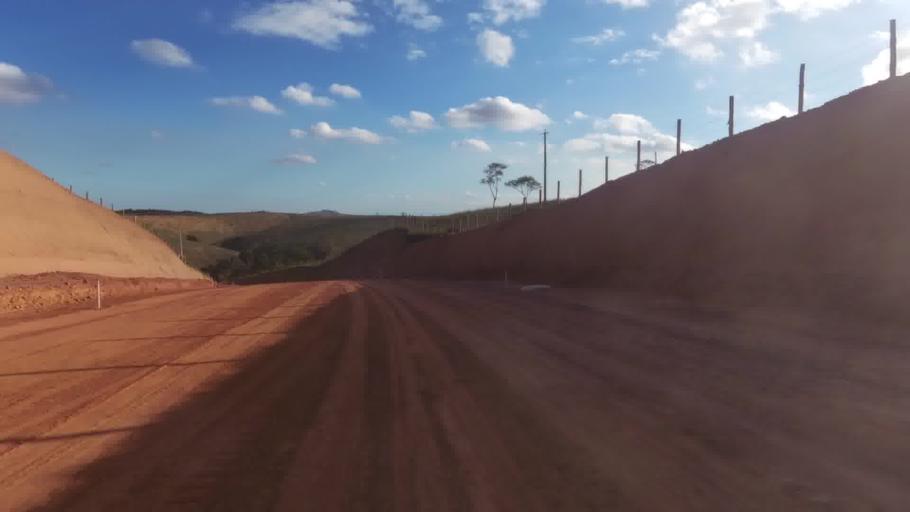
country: BR
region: Espirito Santo
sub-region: Marataizes
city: Marataizes
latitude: -21.1110
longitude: -41.0472
